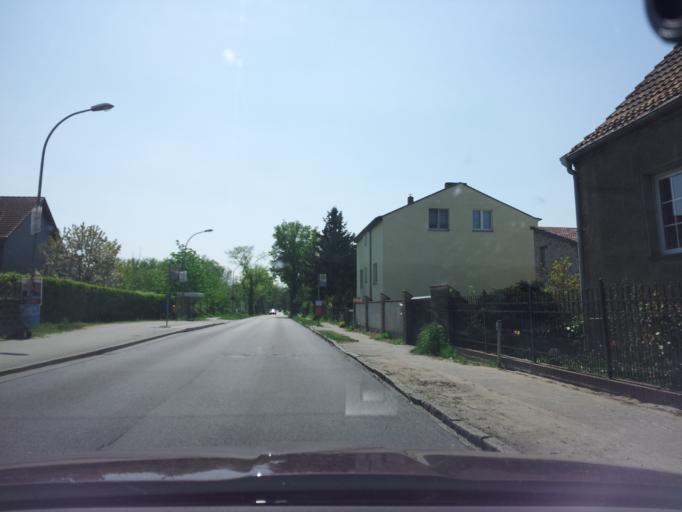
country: DE
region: Brandenburg
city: Stahnsdorf
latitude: 52.3880
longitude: 13.2166
